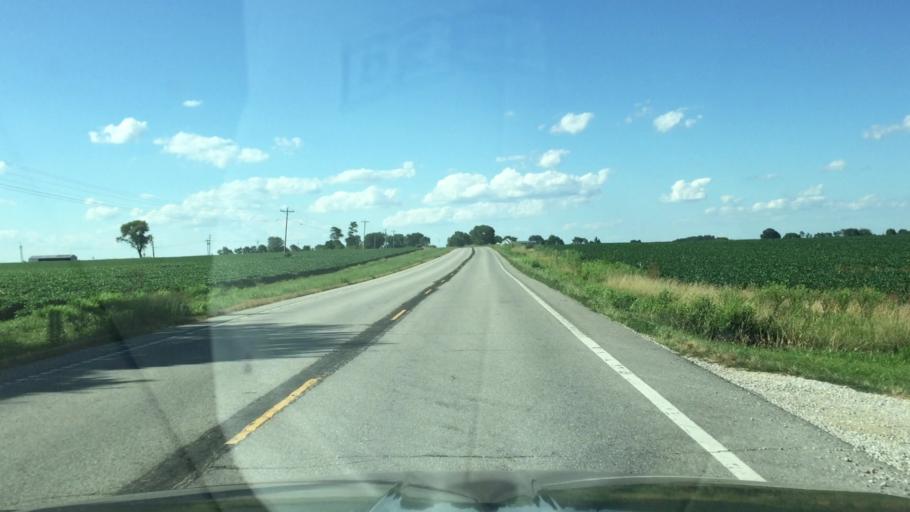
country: US
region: Missouri
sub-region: Moniteau County
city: Tipton
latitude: 38.5998
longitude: -92.7894
